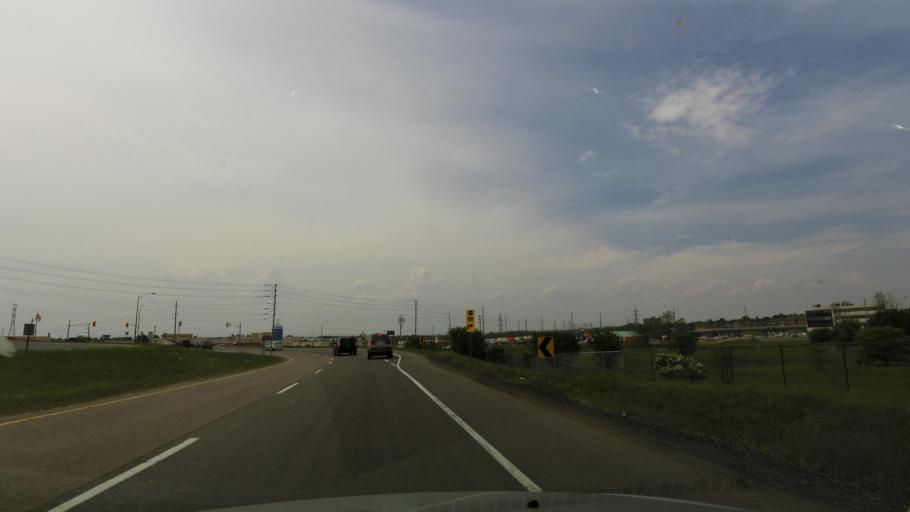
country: CA
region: Ontario
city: Oshawa
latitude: 43.8705
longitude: -78.9039
